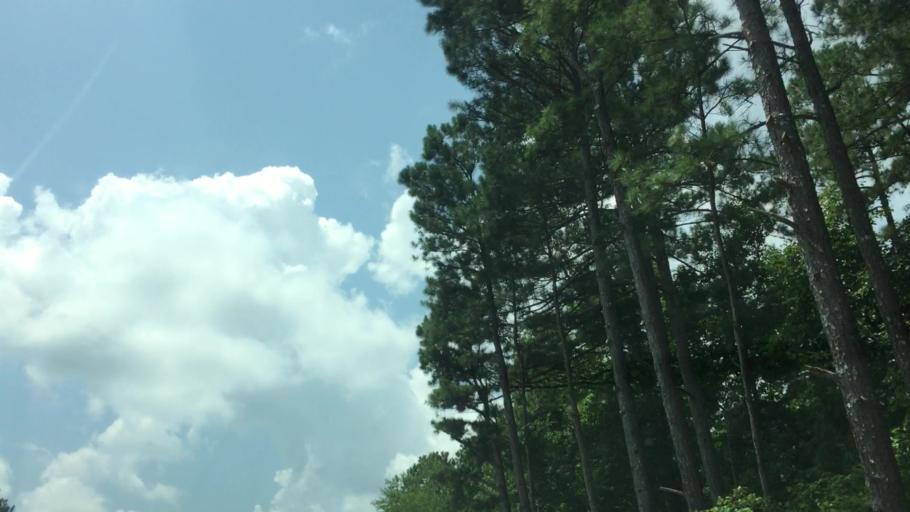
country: US
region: Georgia
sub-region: Carroll County
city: Villa Rica
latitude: 33.6140
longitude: -84.8886
